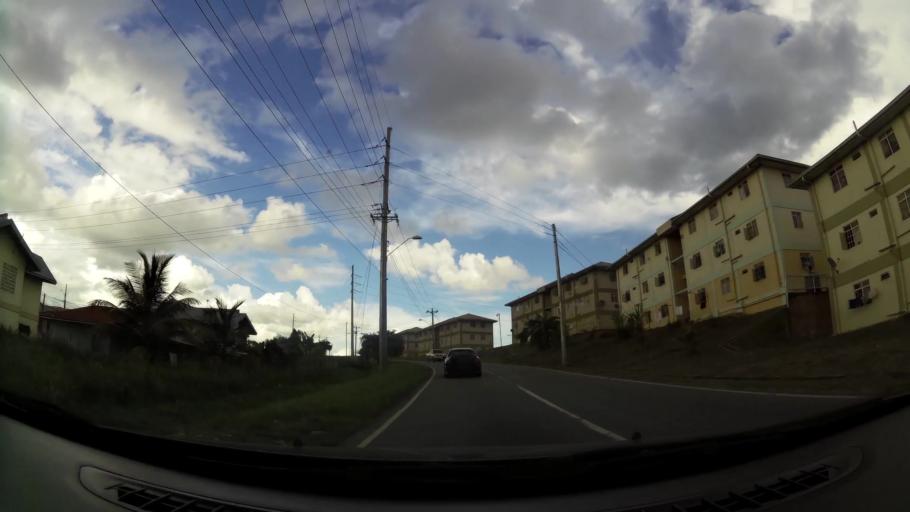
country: TT
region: City of San Fernando
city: Mon Repos
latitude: 10.2654
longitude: -61.4442
